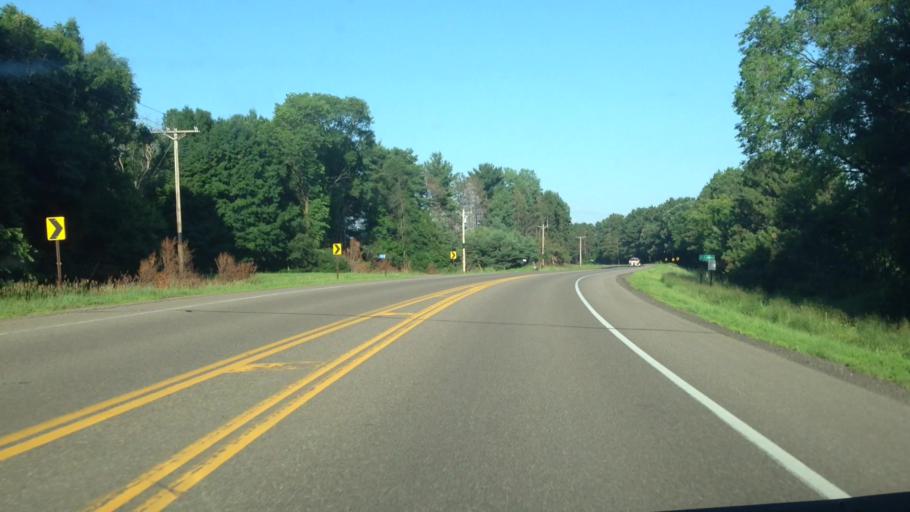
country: US
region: Minnesota
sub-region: Sherburne County
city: Zimmerman
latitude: 45.4445
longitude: -93.6253
